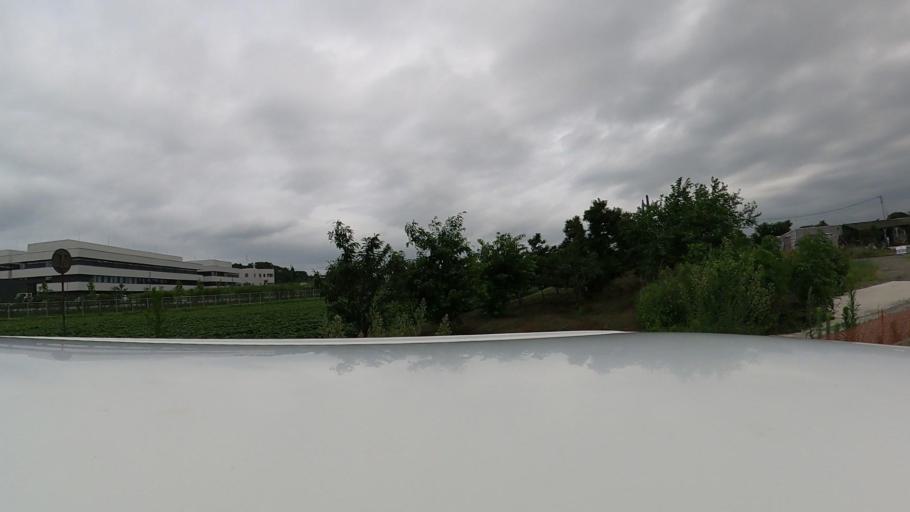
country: JP
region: Kumamoto
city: Ozu
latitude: 32.8347
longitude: 130.8717
